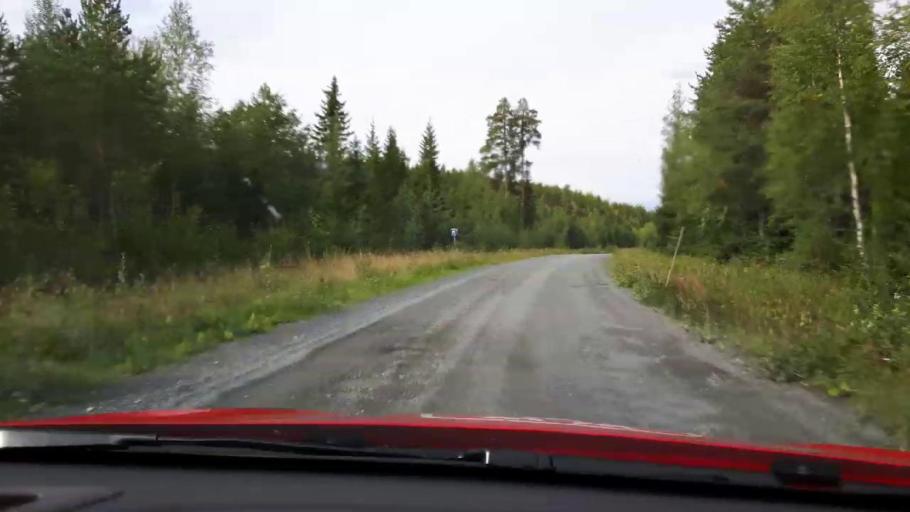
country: SE
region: Jaemtland
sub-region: Are Kommun
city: Jarpen
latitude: 63.2742
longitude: 13.7423
